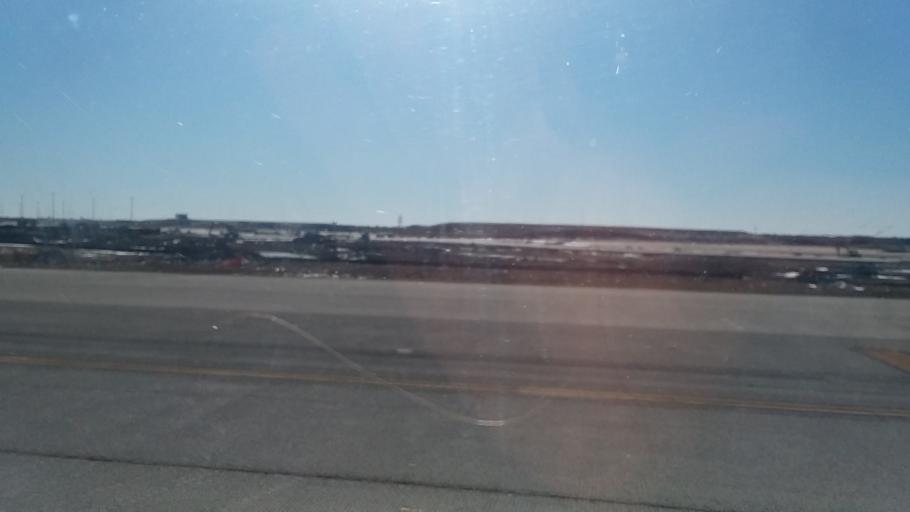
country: US
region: Illinois
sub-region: DuPage County
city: Bensenville
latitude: 41.9861
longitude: -87.9279
